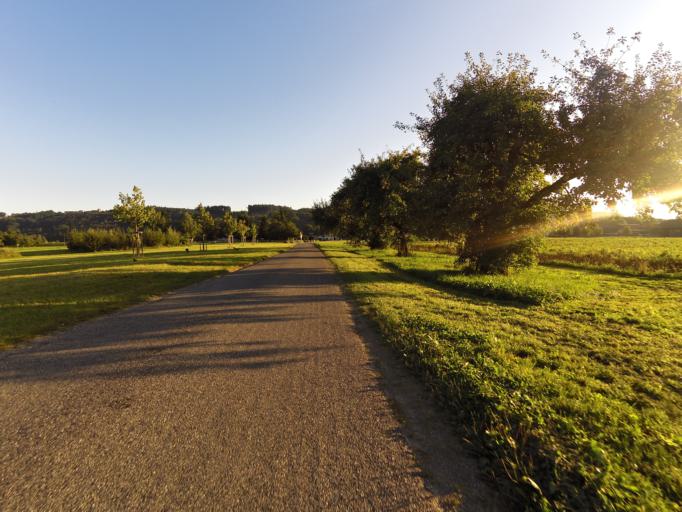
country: CH
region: Thurgau
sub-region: Weinfelden District
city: Wigoltingen
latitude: 47.5861
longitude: 9.0274
